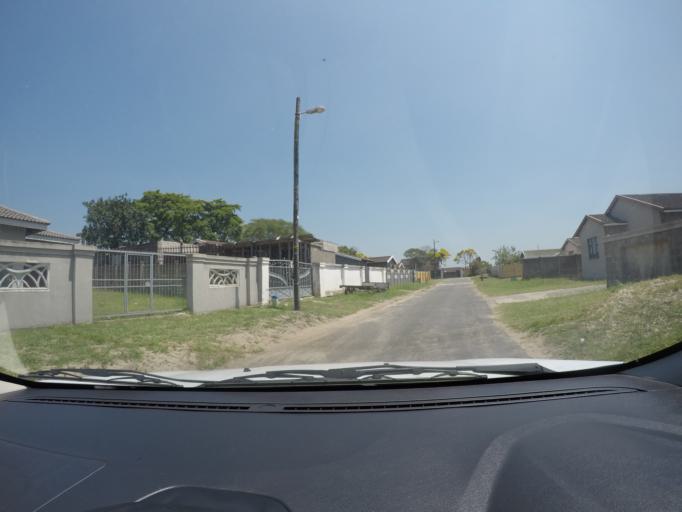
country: ZA
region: KwaZulu-Natal
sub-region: uThungulu District Municipality
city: eSikhawini
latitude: -28.8689
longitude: 31.9179
